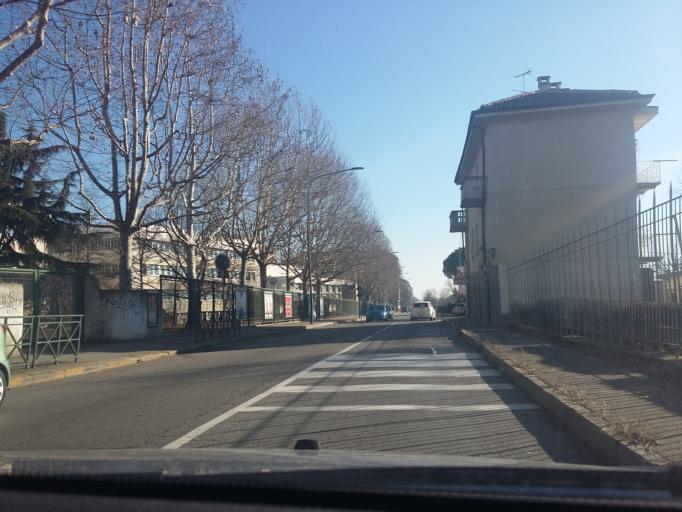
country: IT
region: Piedmont
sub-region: Provincia di Torino
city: Nichelino
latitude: 45.0121
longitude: 7.6288
